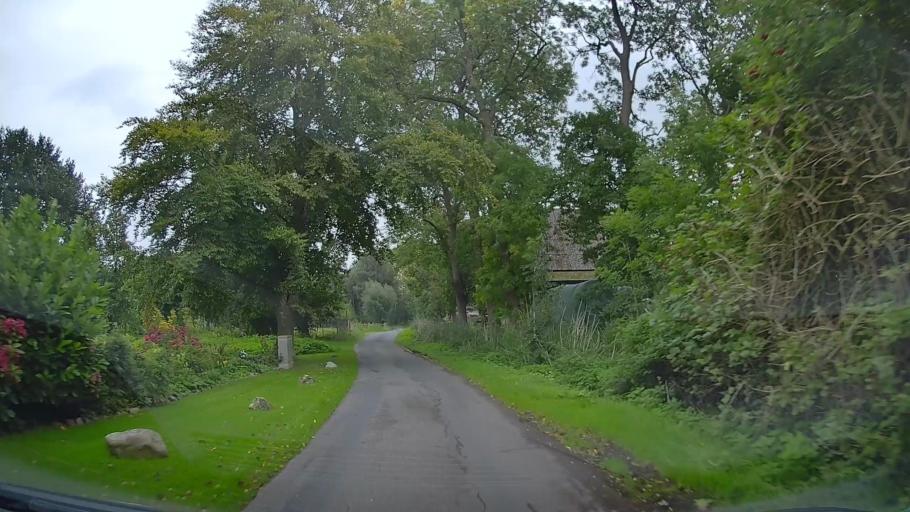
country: DE
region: Lower Saxony
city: Freiburg
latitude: 53.8268
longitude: 9.2653
